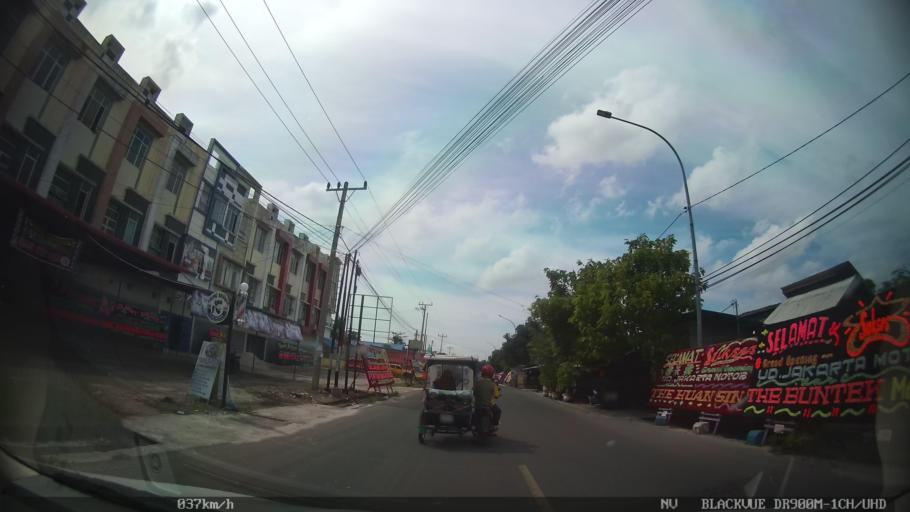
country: ID
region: North Sumatra
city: Percut
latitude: 3.5748
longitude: 98.8678
